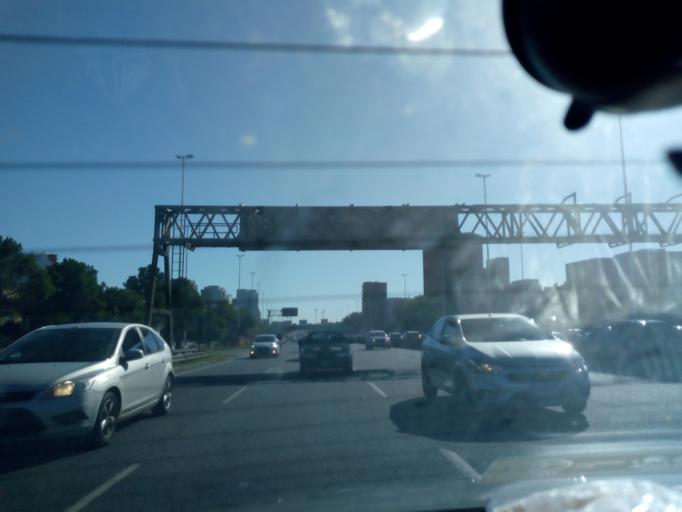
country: AR
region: Buenos Aires
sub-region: Partido de Vicente Lopez
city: Olivos
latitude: -34.5379
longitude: -58.4739
